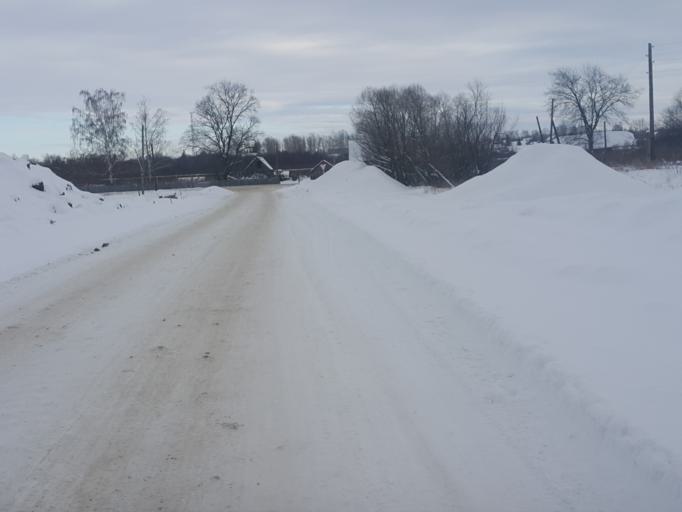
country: RU
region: Tambov
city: Platonovka
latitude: 52.8805
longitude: 41.8754
